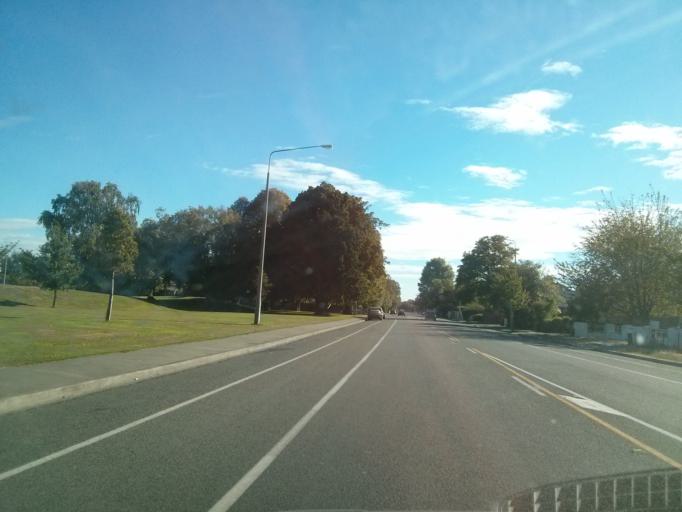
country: NZ
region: Canterbury
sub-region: Christchurch City
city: Christchurch
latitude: -43.5257
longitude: 172.5876
